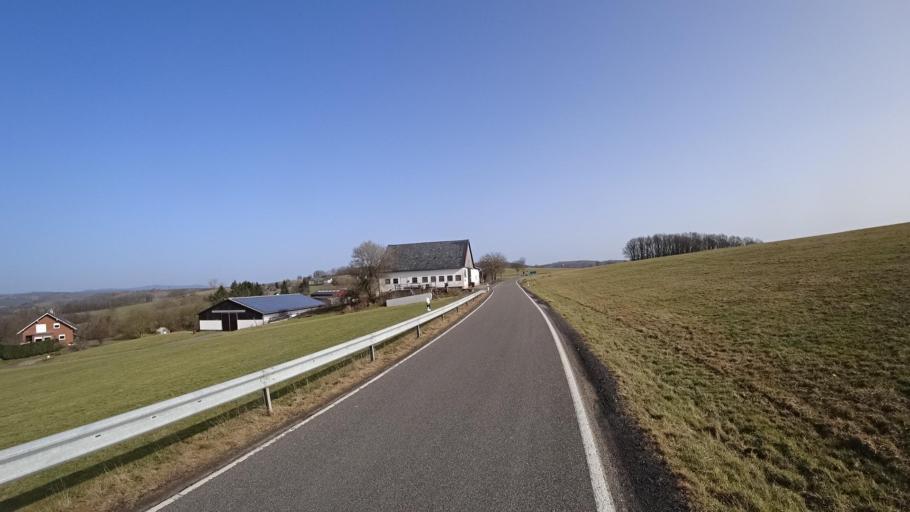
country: DE
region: Rheinland-Pfalz
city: Mittelhof
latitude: 50.7712
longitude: 7.7789
